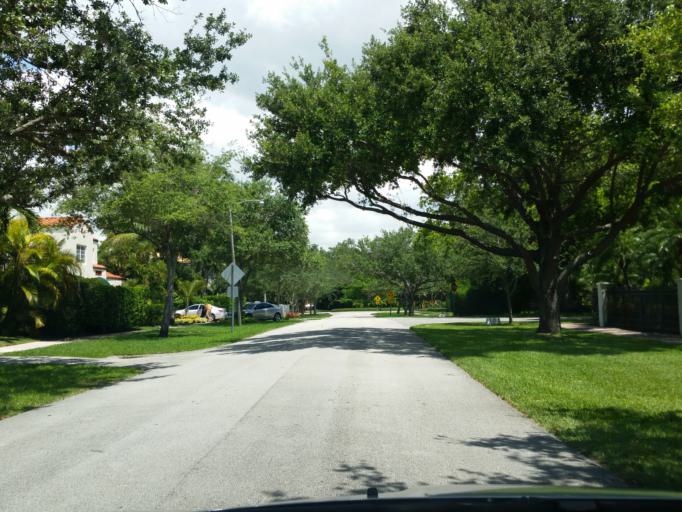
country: US
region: Florida
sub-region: Miami-Dade County
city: Coconut Grove
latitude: 25.7099
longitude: -80.2625
